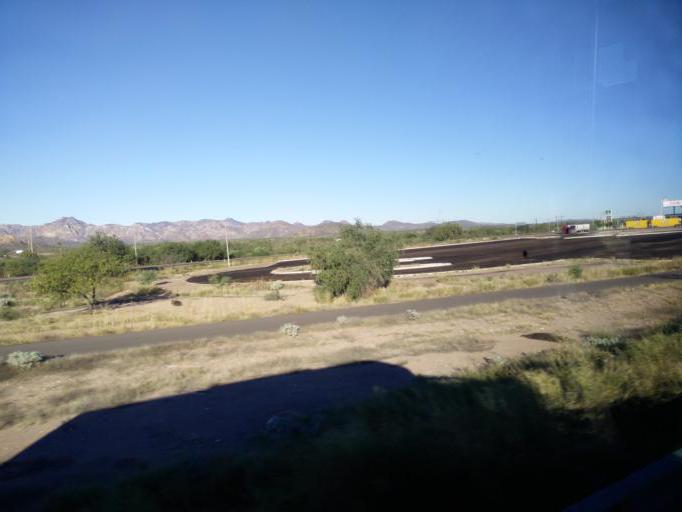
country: MX
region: Sonora
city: Heroica Guaymas
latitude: 28.0404
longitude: -110.9379
